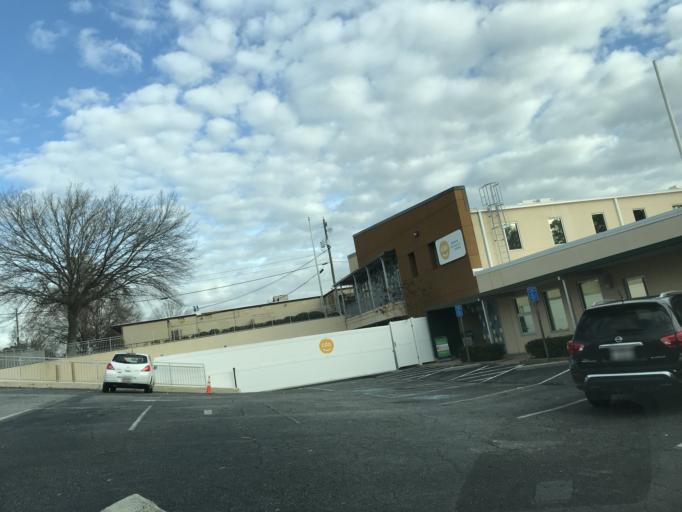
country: US
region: Georgia
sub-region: Fulton County
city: Roswell
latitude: 34.0182
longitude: -84.3598
